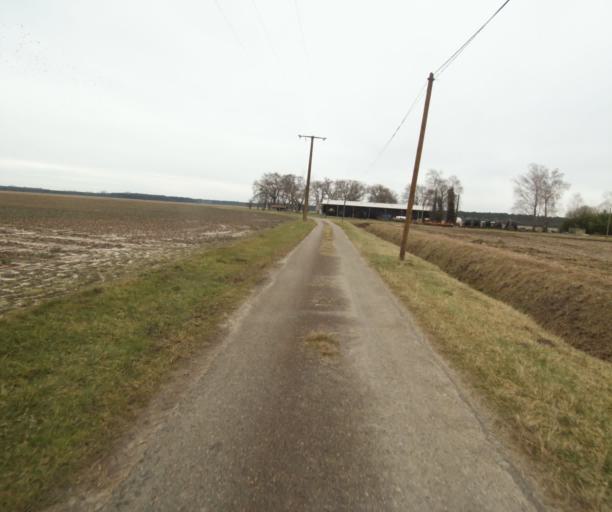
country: FR
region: Aquitaine
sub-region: Departement des Landes
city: Gabarret
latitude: 44.0161
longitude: -0.0135
